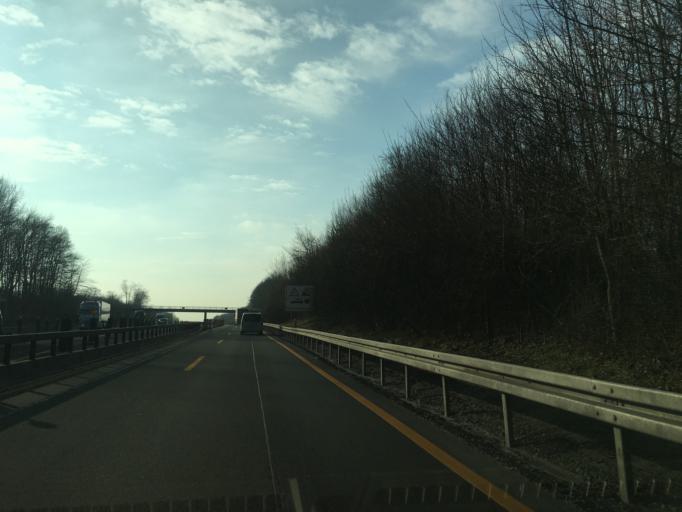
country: DE
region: North Rhine-Westphalia
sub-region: Regierungsbezirk Munster
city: Tecklenburg
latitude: 52.2100
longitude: 7.8403
